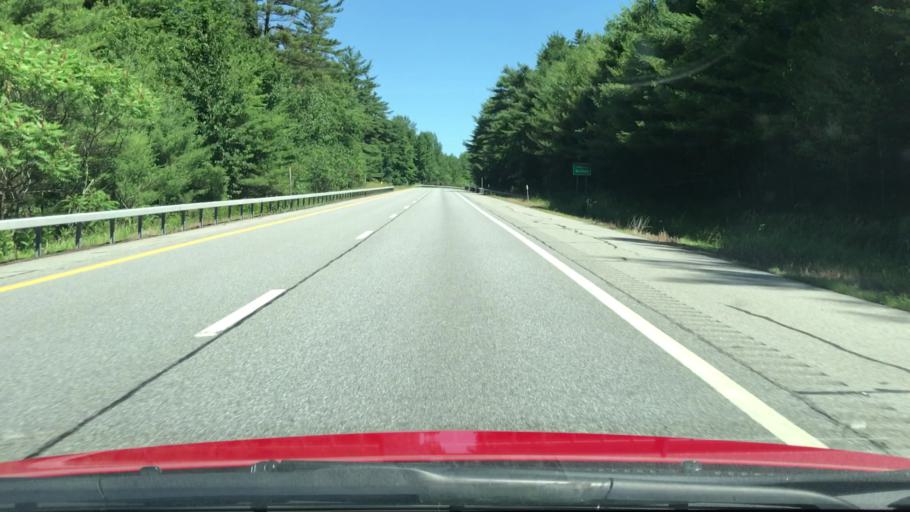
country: US
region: New York
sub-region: Warren County
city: Warrensburg
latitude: 43.5080
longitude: -73.7432
